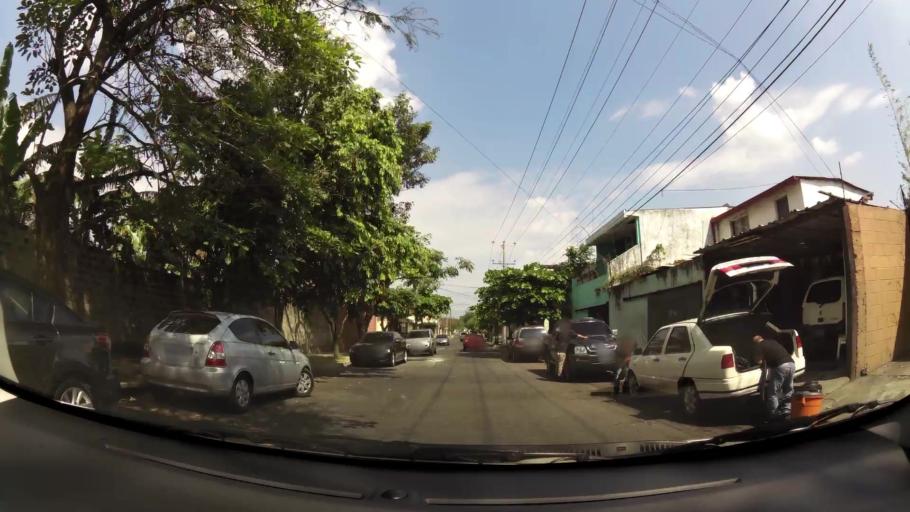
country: SV
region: San Salvador
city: Mejicanos
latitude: 13.7112
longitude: -89.2226
